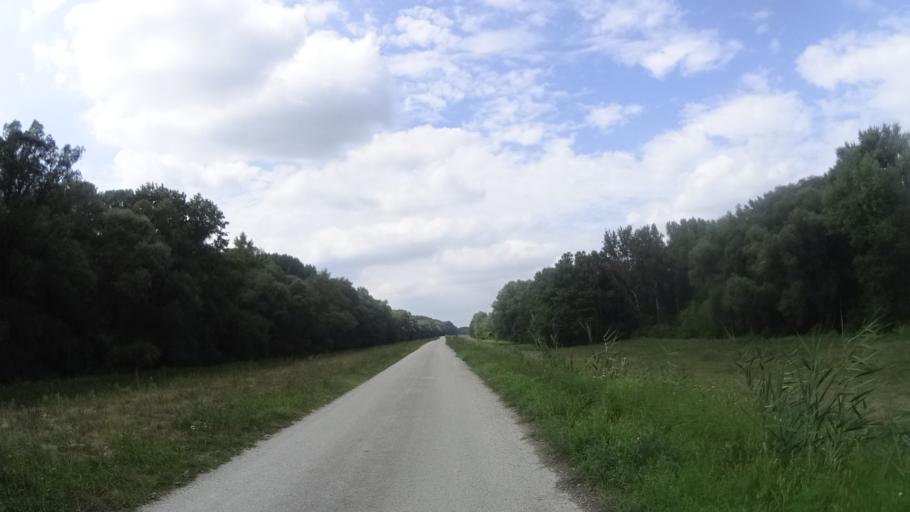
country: SK
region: Trnavsky
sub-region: Okres Dunajska Streda
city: Velky Meder
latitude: 47.7731
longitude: 17.7126
